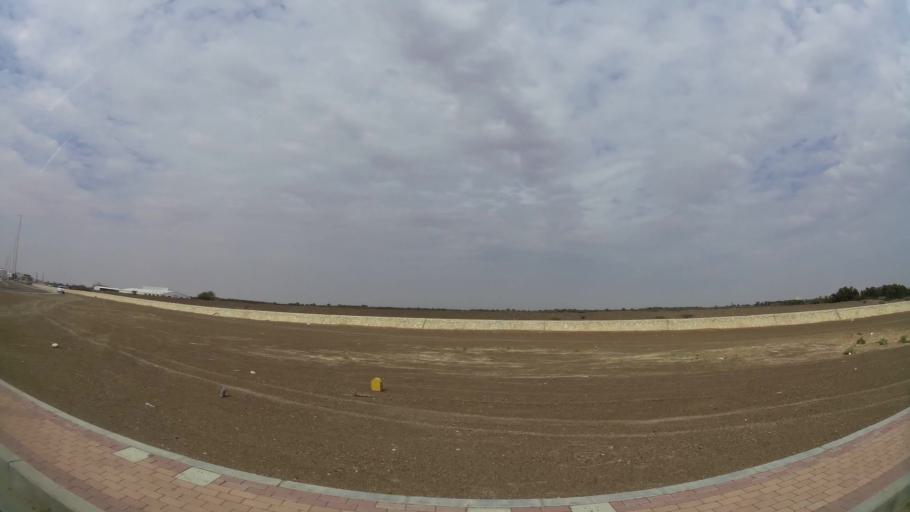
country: AE
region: Abu Dhabi
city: Al Ain
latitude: 24.1957
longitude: 55.8133
